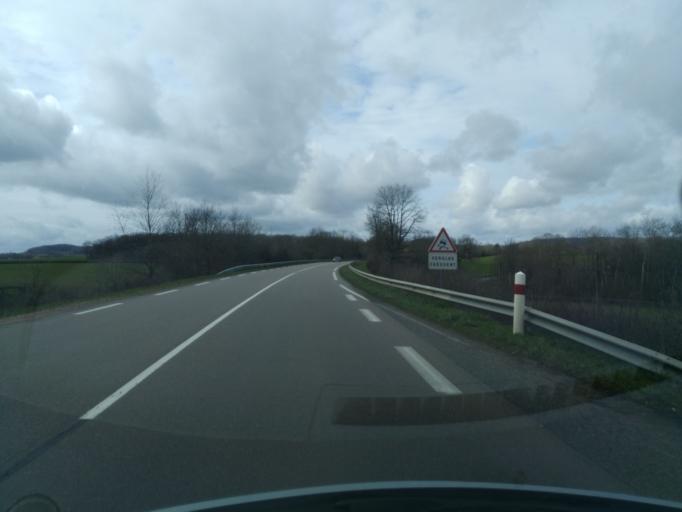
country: FR
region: Bourgogne
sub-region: Departement de Saone-et-Loire
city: Torcy
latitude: 46.7679
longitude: 4.4353
